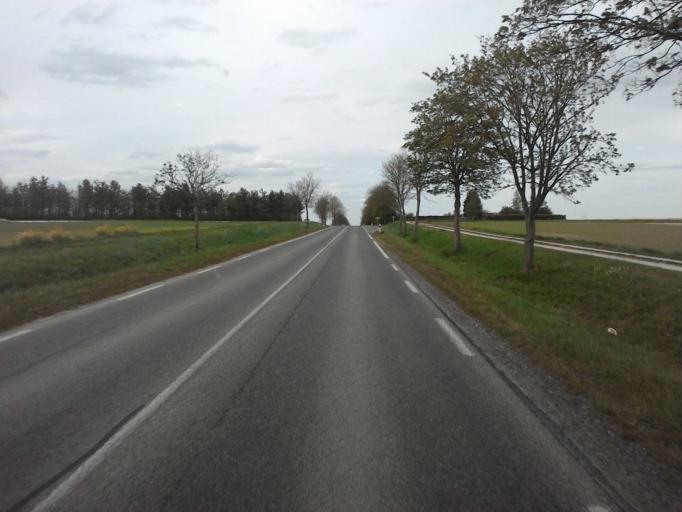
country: FR
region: Champagne-Ardenne
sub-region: Departement de l'Aube
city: Mailly-le-Camp
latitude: 48.7432
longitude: 4.2072
